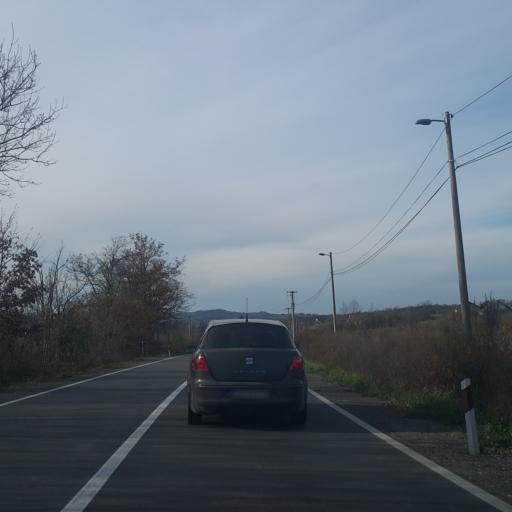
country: RS
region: Central Serbia
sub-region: Sumadijski Okrug
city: Arangelovac
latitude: 44.3375
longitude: 20.4267
